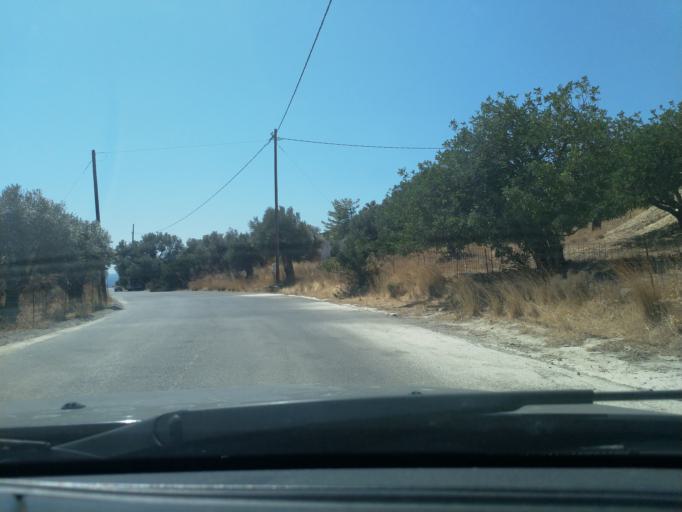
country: GR
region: Crete
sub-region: Nomos Rethymnis
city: Agia Galini
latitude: 35.1236
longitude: 24.5561
